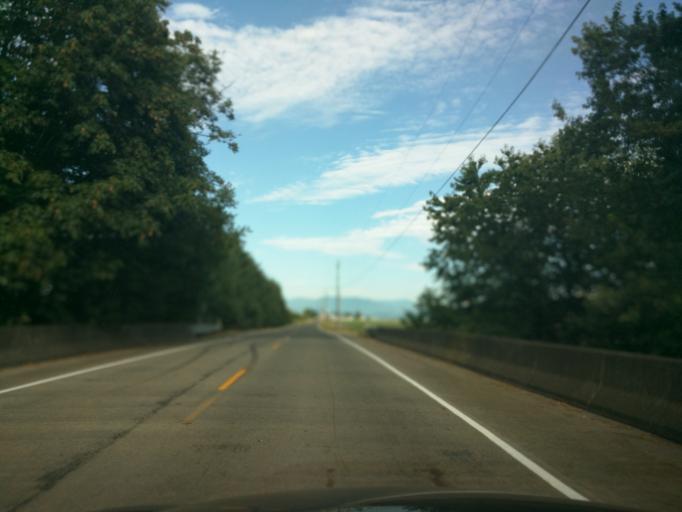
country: US
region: Washington
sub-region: Whatcom County
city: Lynden
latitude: 48.9934
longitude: -122.5096
